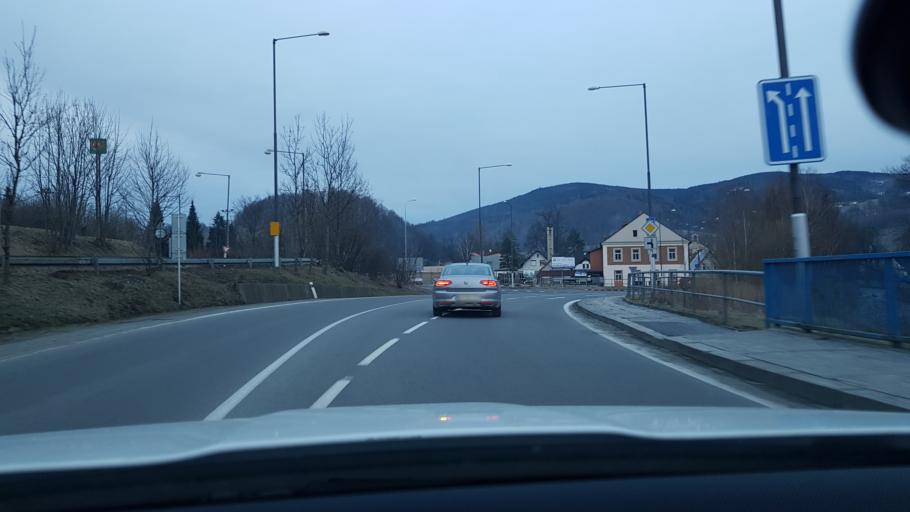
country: CZ
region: Olomoucky
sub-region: Okres Jesenik
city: Jesenik
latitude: 50.2131
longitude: 17.2006
